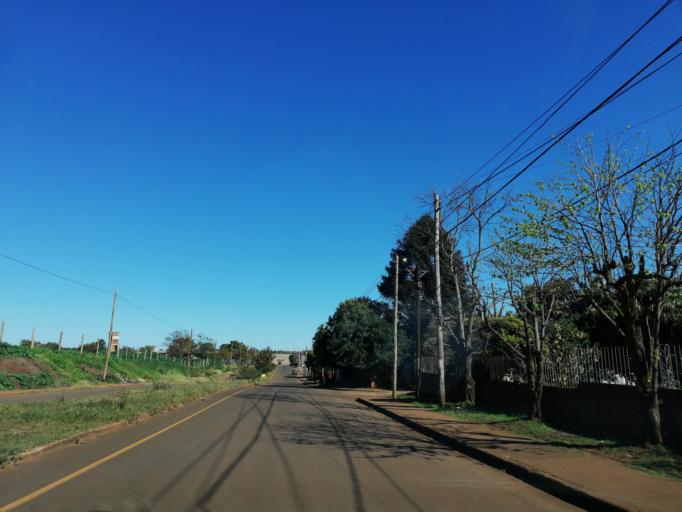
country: AR
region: Misiones
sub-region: Departamento de Capital
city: Posadas
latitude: -27.3930
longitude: -55.9434
